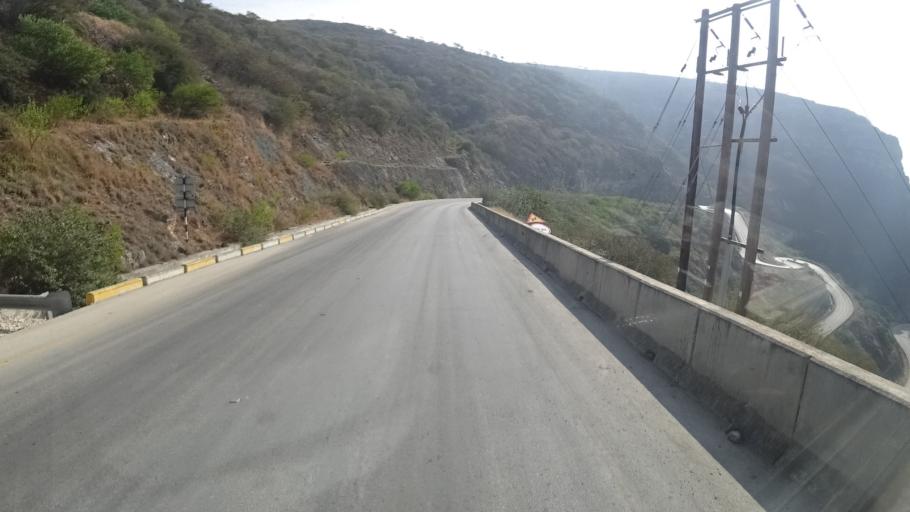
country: YE
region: Al Mahrah
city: Hawf
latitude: 16.7085
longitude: 53.1444
